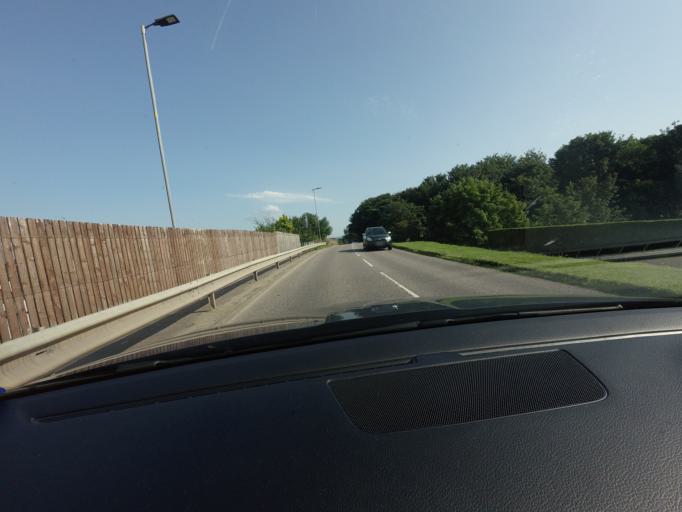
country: GB
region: Scotland
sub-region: Highland
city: Alness
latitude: 57.6942
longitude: -4.2452
